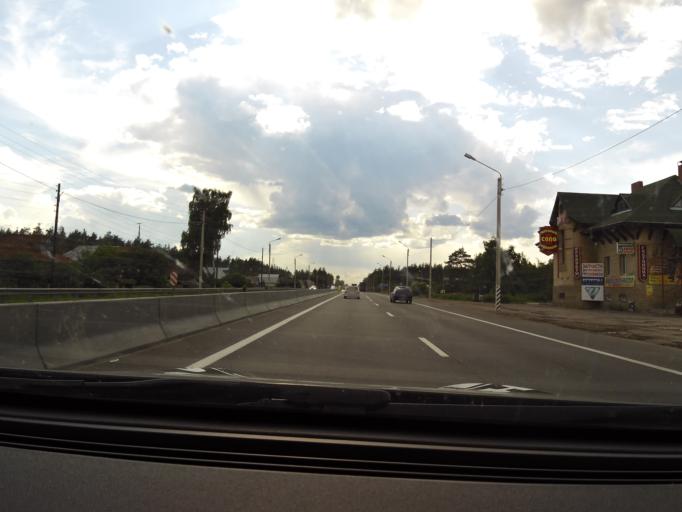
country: RU
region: Nizjnij Novgorod
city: Pyra
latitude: 56.2926
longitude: 43.3365
